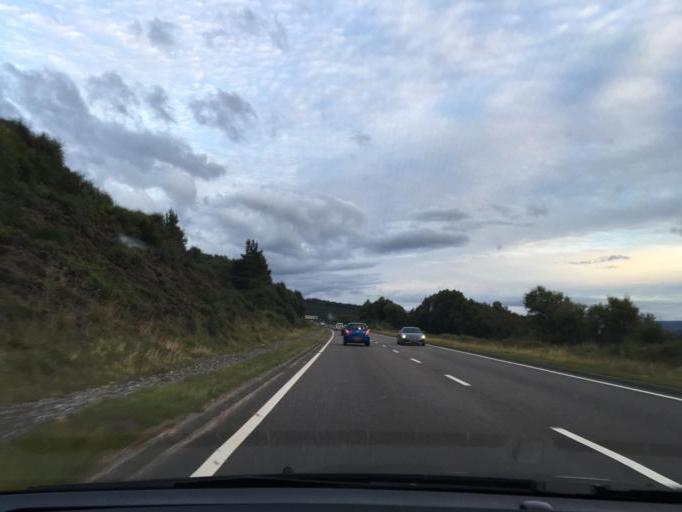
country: GB
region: Scotland
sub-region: Highland
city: Aviemore
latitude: 57.2982
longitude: -3.9228
